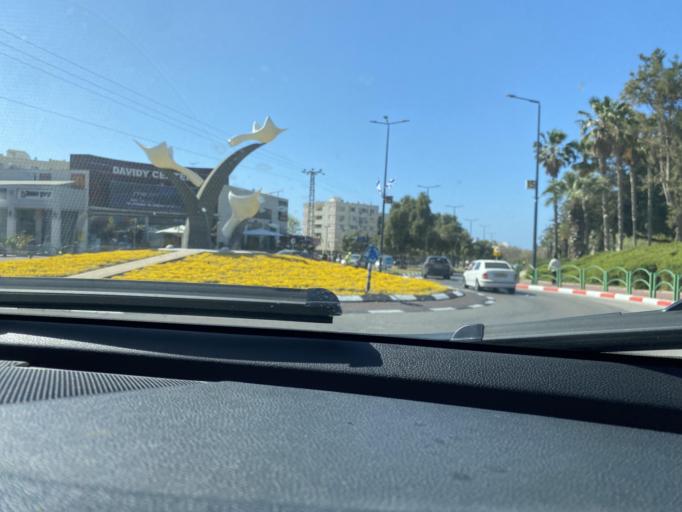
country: IL
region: Southern District
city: Ashqelon
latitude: 31.6809
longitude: 34.5710
